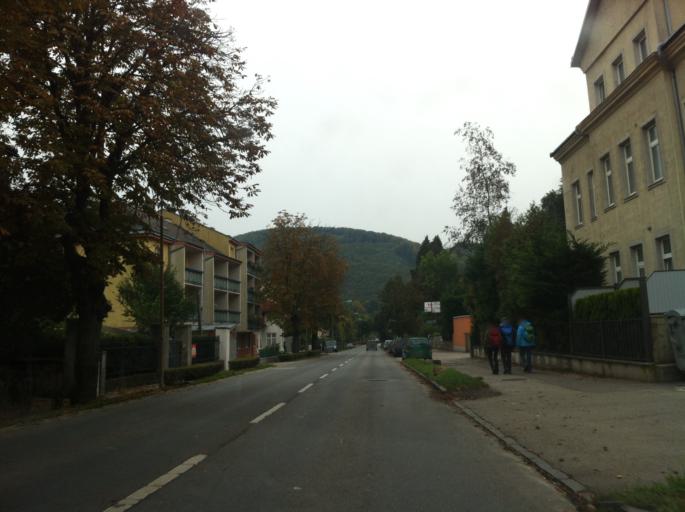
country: AT
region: Lower Austria
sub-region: Politischer Bezirk Wien-Umgebung
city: Purkersdorf
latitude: 48.2132
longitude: 16.1718
